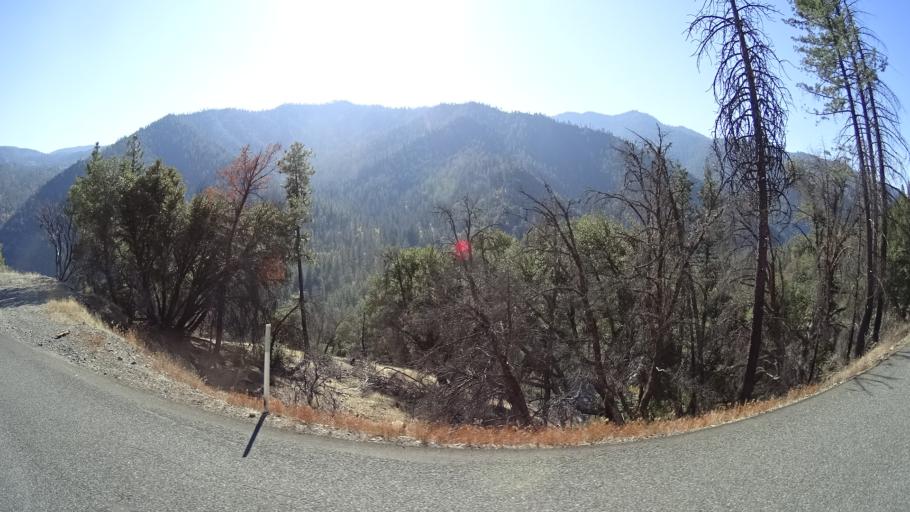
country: US
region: California
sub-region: Siskiyou County
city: Happy Camp
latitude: 41.7097
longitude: -123.0288
